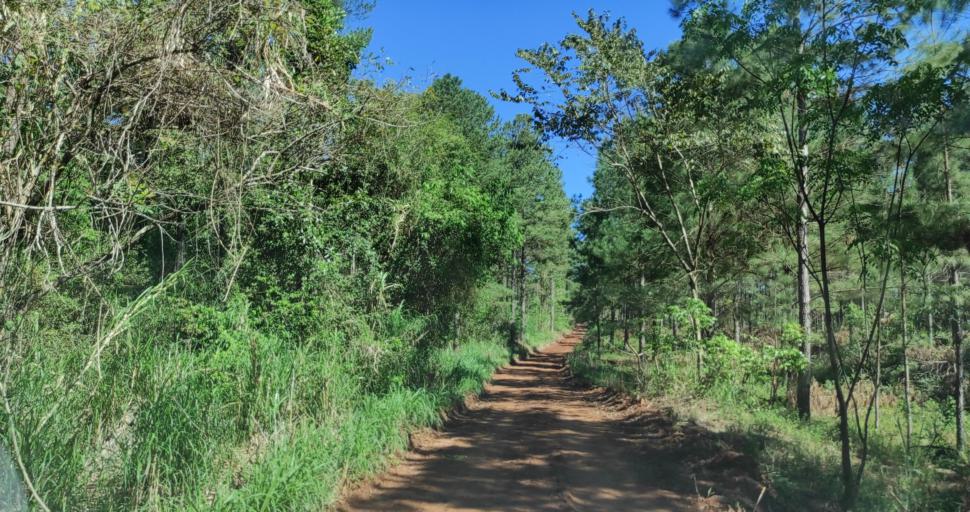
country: AR
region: Misiones
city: Ruiz de Montoya
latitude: -26.9448
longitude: -54.9802
